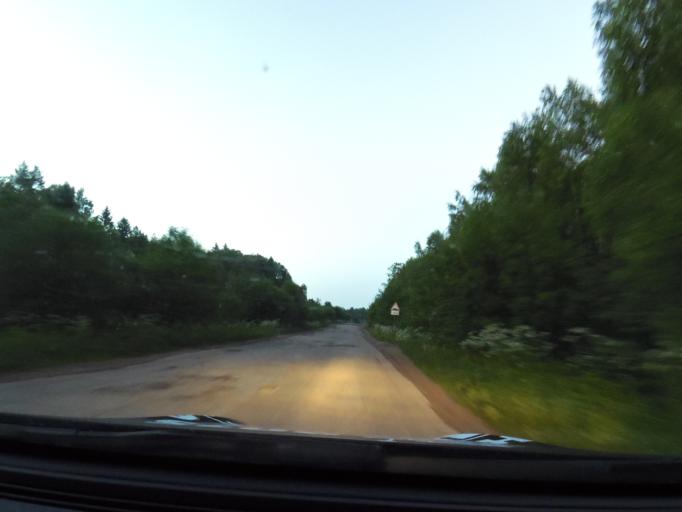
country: RU
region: Vologda
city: Vytegra
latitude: 61.0022
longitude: 36.2969
